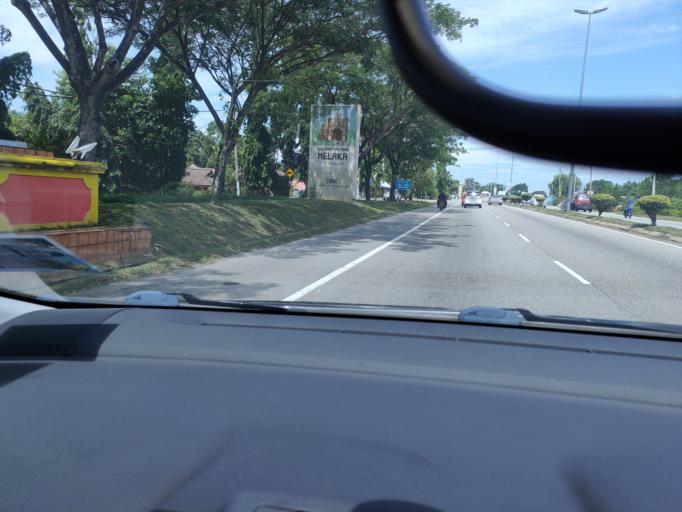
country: MY
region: Melaka
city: Batu Berendam
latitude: 2.2625
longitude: 102.2200
